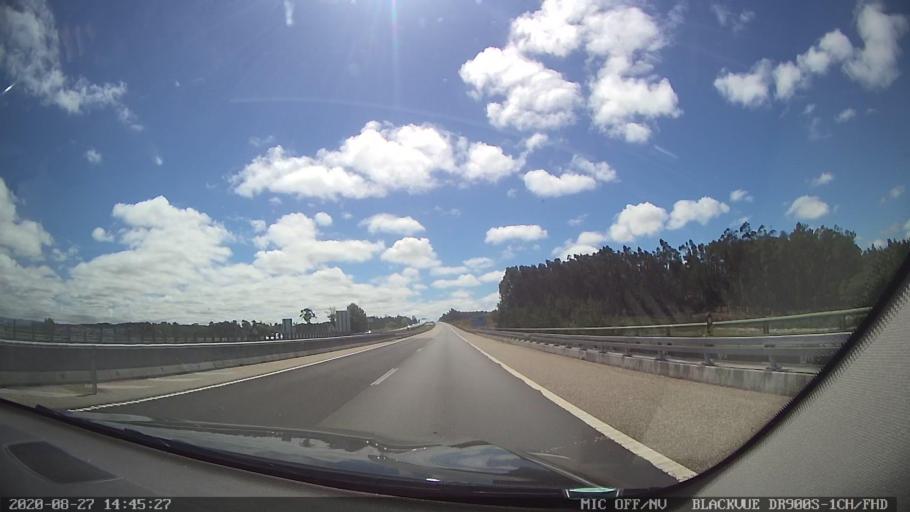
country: PT
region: Leiria
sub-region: Leiria
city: Amor
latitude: 39.8065
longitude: -8.8477
